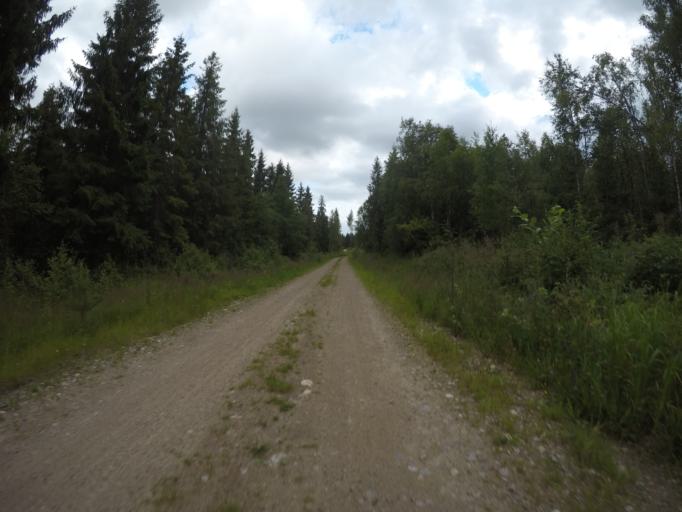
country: SE
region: Vaermland
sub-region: Filipstads Kommun
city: Lesjofors
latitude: 60.1575
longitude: 14.3902
